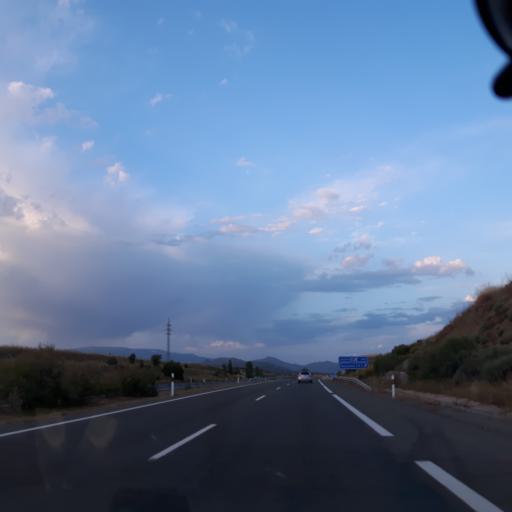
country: ES
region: Castille and Leon
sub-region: Provincia de Salamanca
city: Guijuelo
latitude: 40.5361
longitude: -5.6647
